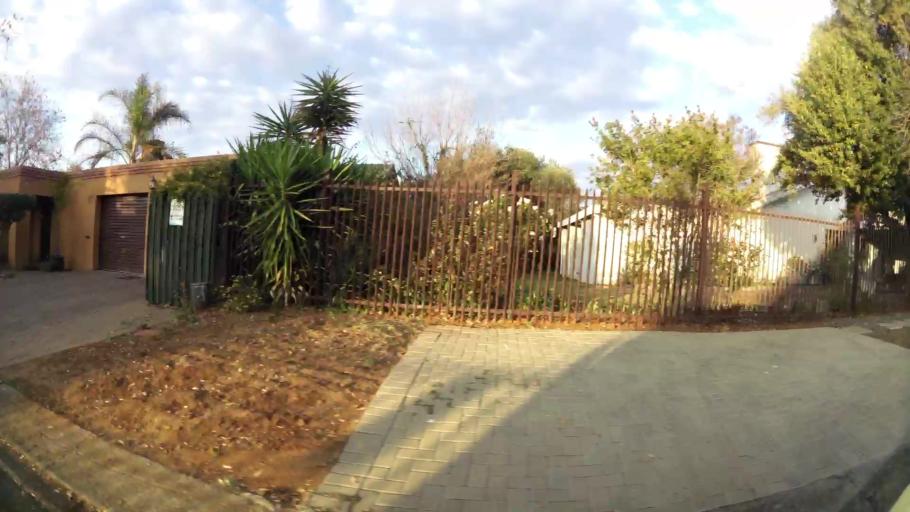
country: ZA
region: Orange Free State
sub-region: Mangaung Metropolitan Municipality
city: Bloemfontein
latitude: -29.1400
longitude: 26.1828
